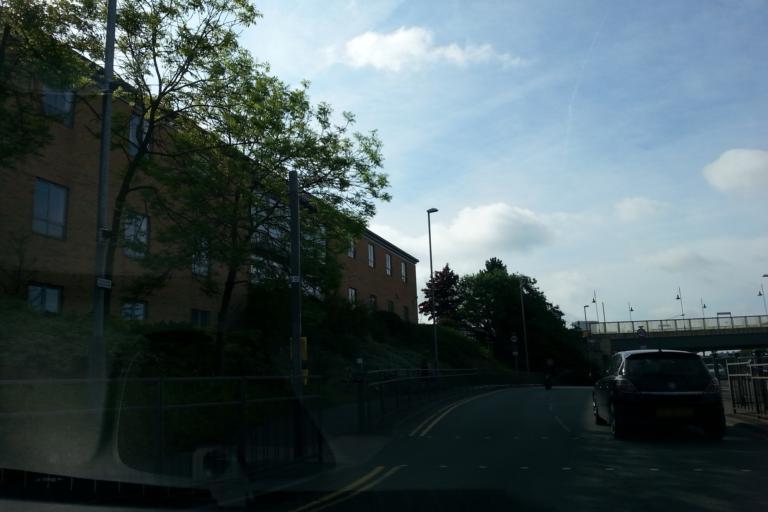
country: GB
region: England
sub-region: Nottinghamshire
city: Mansfield
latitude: 53.1426
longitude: -1.1998
